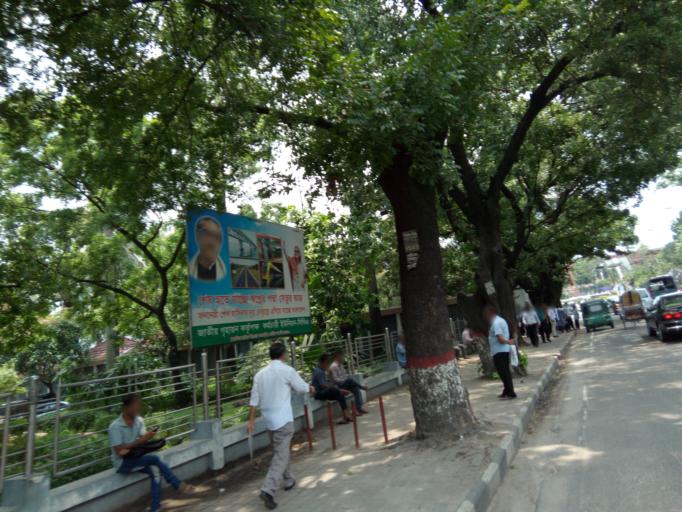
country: BD
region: Dhaka
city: Paltan
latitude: 23.7310
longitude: 90.4050
